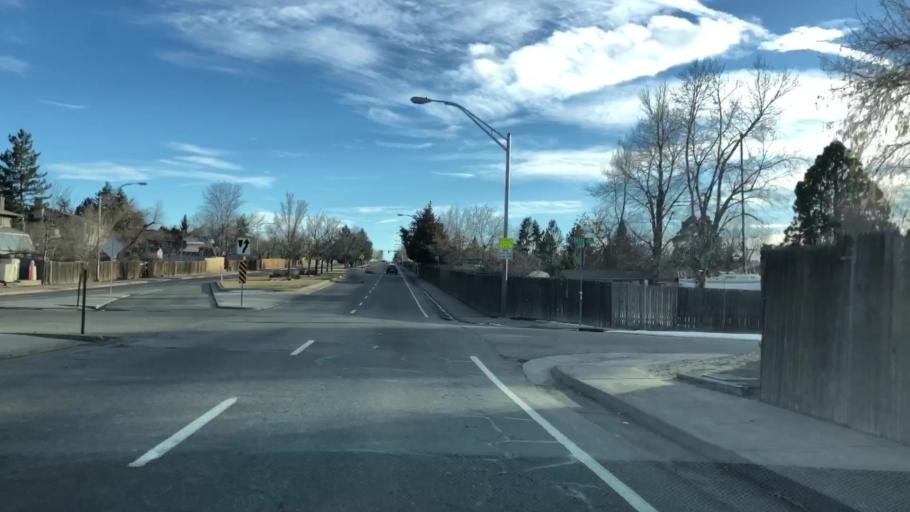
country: US
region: Colorado
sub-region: Adams County
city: Aurora
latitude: 39.6636
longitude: -104.7913
